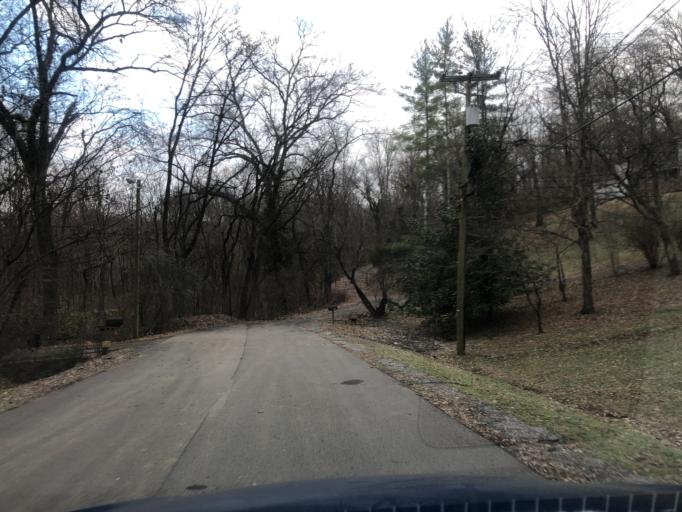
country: US
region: Tennessee
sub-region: Davidson County
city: Belle Meade
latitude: 36.1008
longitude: -86.9386
